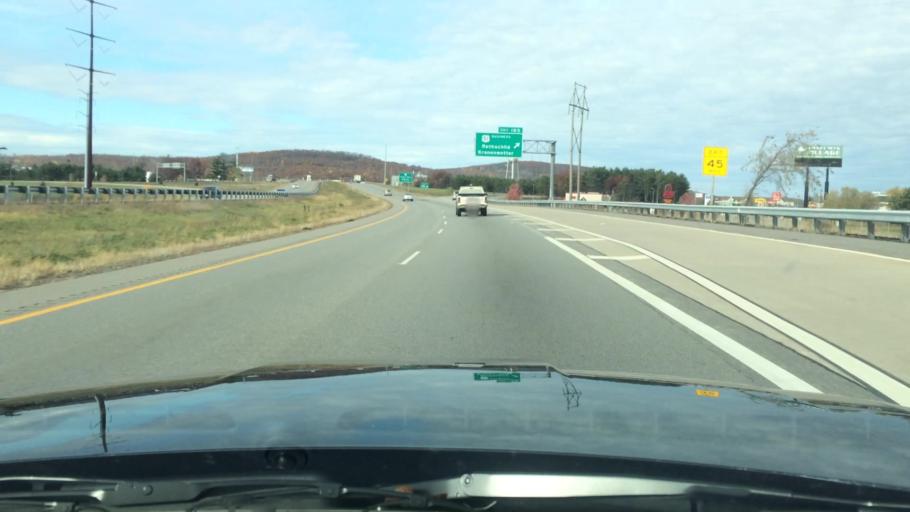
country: US
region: Wisconsin
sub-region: Marathon County
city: Evergreen
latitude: 44.8592
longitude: -89.6377
